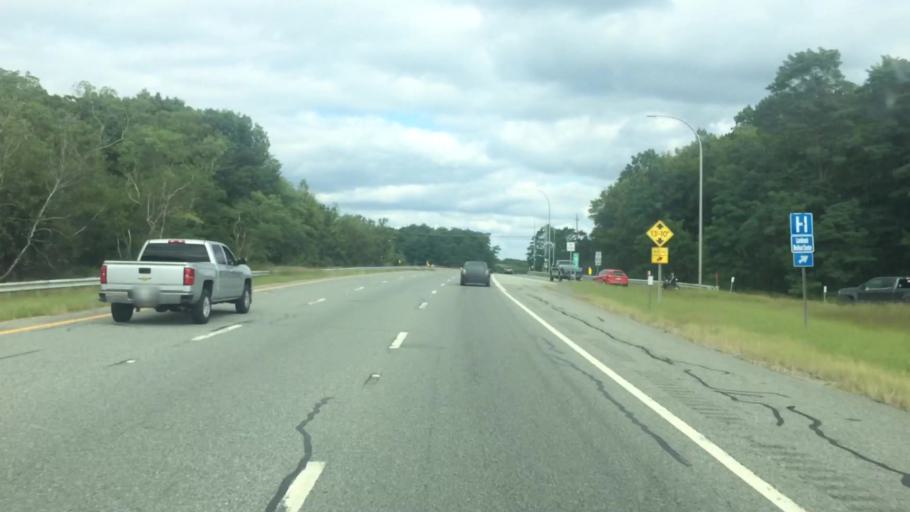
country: US
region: Rhode Island
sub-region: Providence County
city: Cumberland Hill
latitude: 41.9425
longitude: -71.4784
